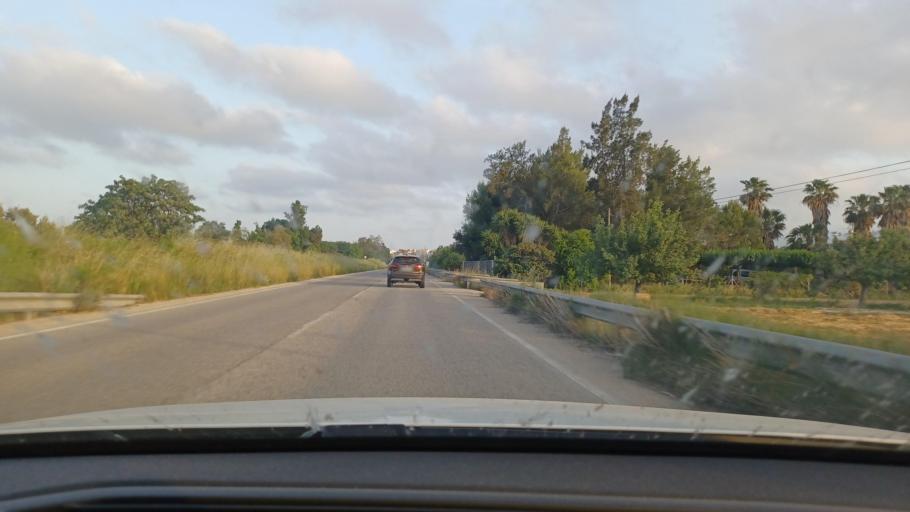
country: ES
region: Catalonia
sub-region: Provincia de Tarragona
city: Amposta
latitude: 40.7238
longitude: 0.5728
